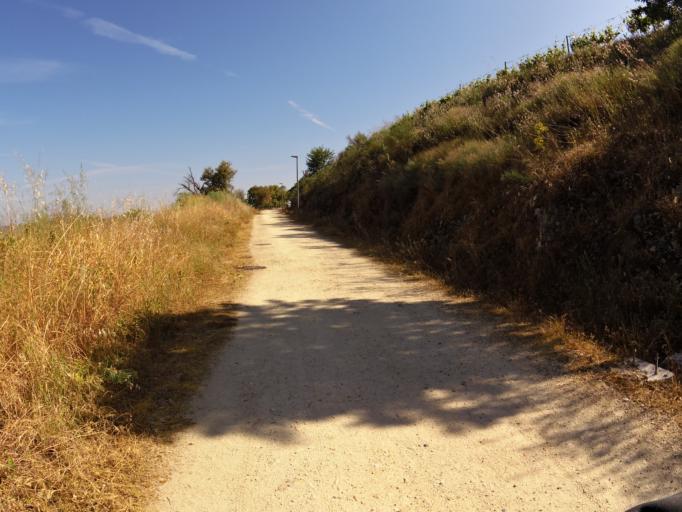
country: PT
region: Braganca
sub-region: Torre de Moncorvo
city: Torre de Moncorvo
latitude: 41.1803
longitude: -7.0341
